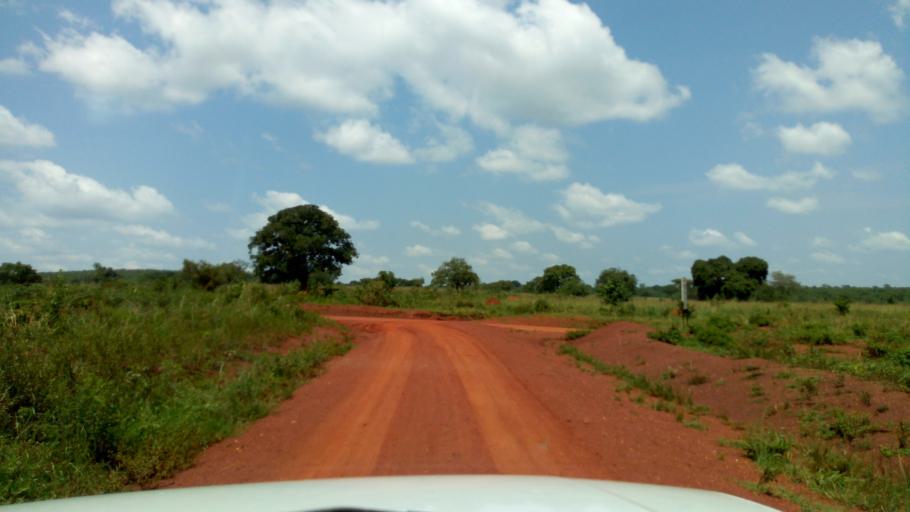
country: UG
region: Western Region
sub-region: Masindi District
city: Masindi
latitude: 1.7319
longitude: 31.8848
